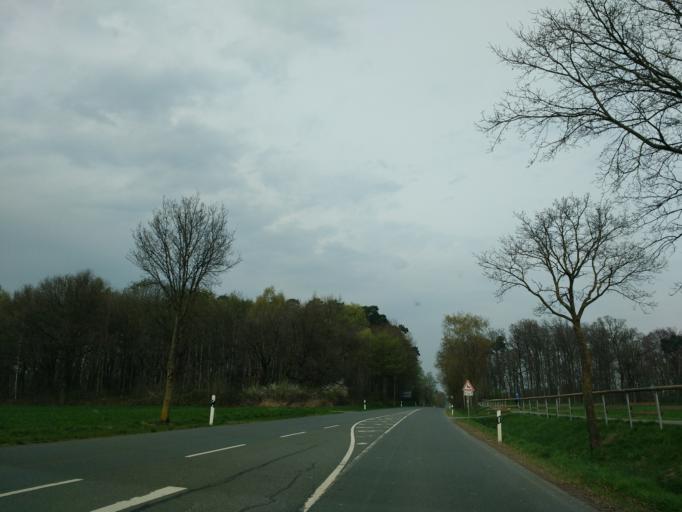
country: DE
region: North Rhine-Westphalia
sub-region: Regierungsbezirk Detmold
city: Salzkotten
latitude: 51.7122
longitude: 8.6620
